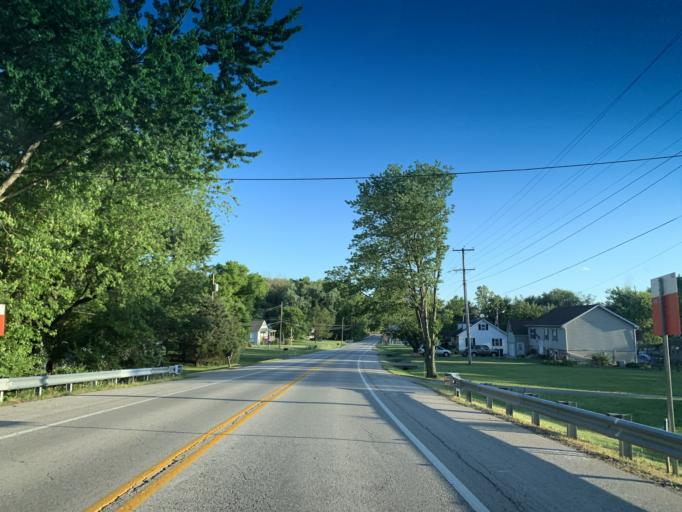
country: US
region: Maryland
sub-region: Cecil County
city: Elkton
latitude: 39.6411
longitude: -75.8125
